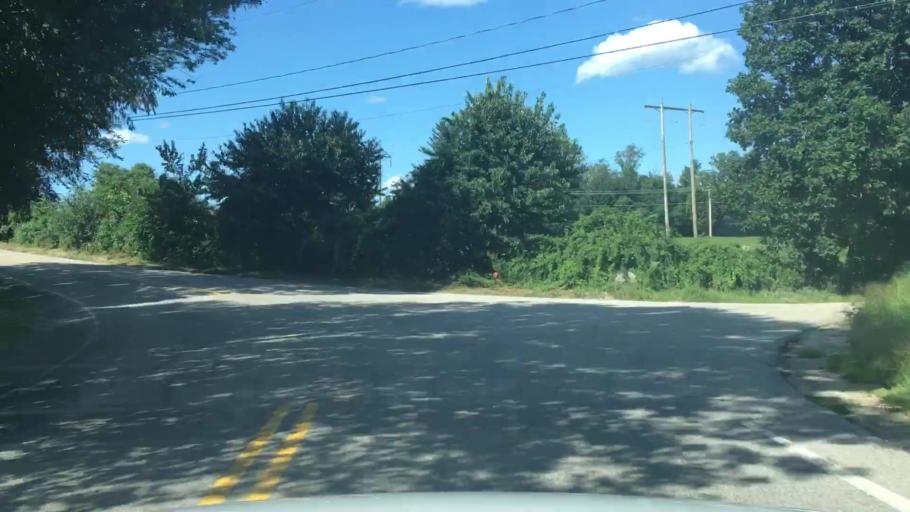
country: US
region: New Hampshire
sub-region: Strafford County
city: Dover
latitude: 43.1874
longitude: -70.8559
